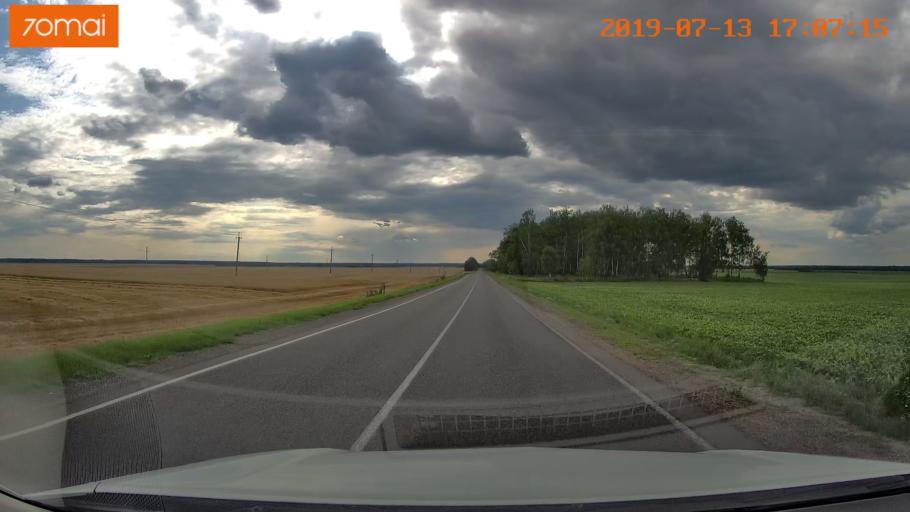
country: BY
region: Mogilev
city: Kirawsk
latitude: 53.2680
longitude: 29.3351
